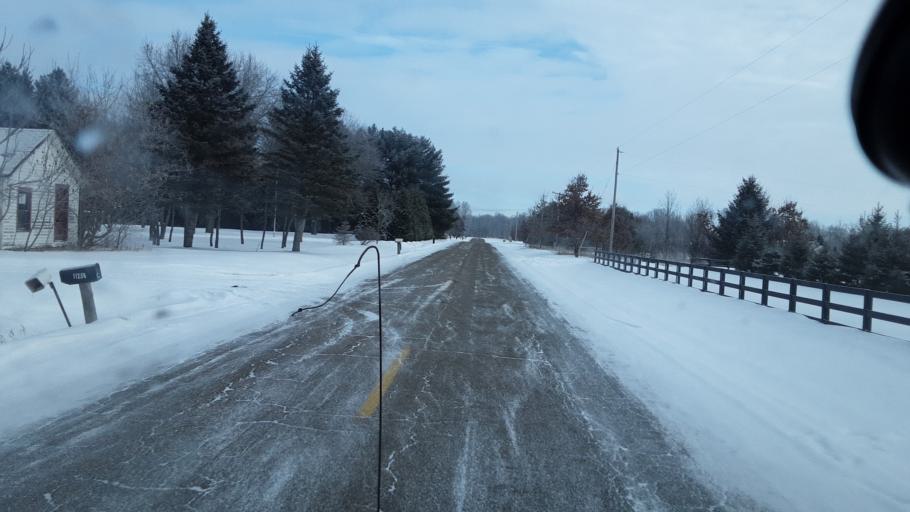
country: US
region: Michigan
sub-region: Ingham County
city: Leslie
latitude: 42.3976
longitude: -84.4879
